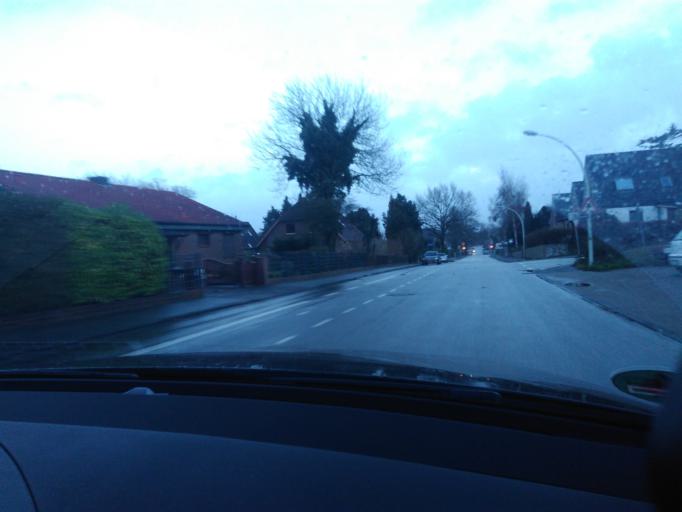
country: DE
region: Schleswig-Holstein
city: Altenholz
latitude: 54.3953
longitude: 10.1625
